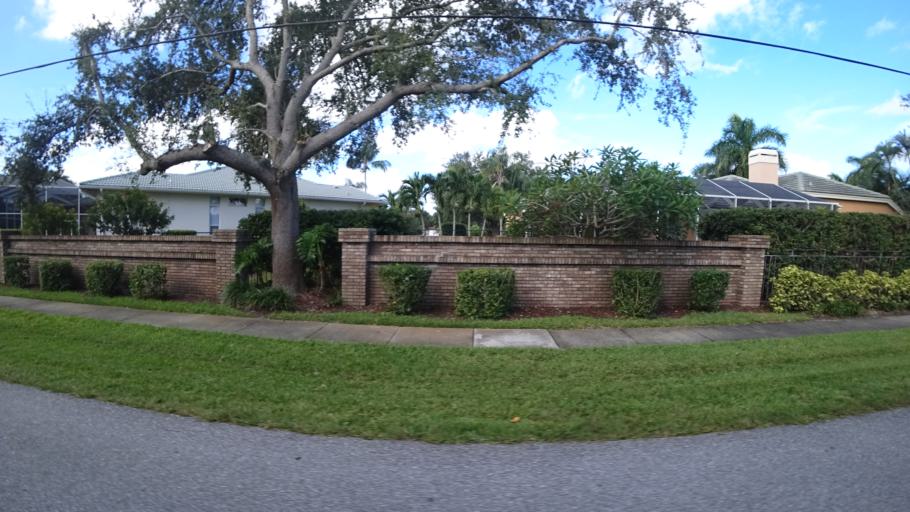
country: US
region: Florida
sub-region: Manatee County
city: West Bradenton
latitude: 27.5150
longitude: -82.6446
